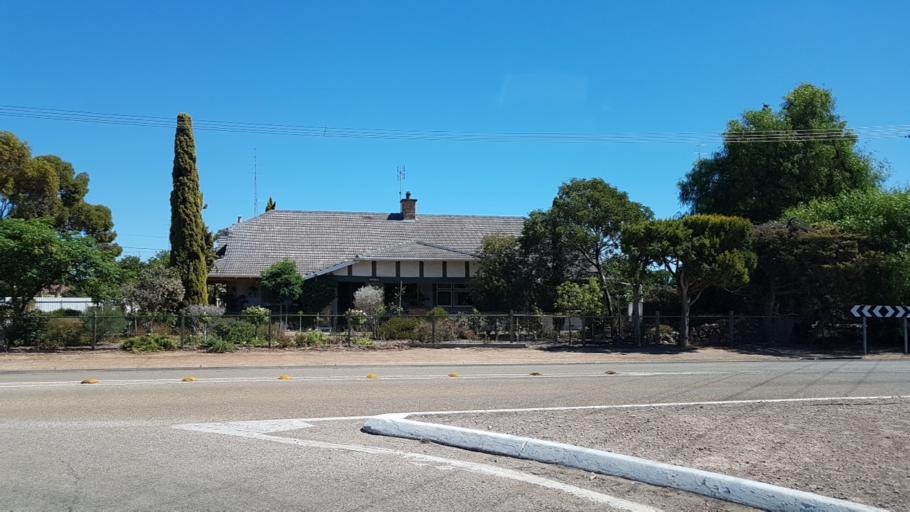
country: AU
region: South Australia
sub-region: Copper Coast
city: Kadina
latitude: -33.9602
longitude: 137.7248
